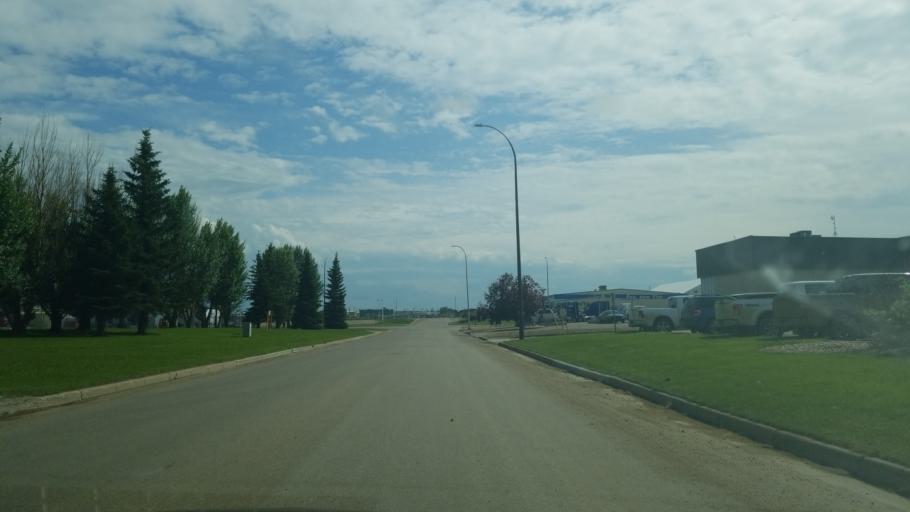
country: CA
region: Saskatchewan
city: Lloydminster
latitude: 53.2879
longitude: -110.0368
